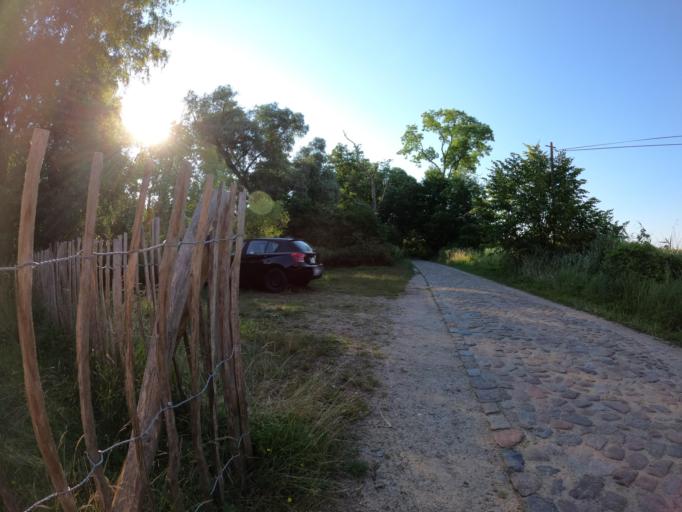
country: DE
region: Brandenburg
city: Tantow
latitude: 53.2518
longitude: 14.3611
